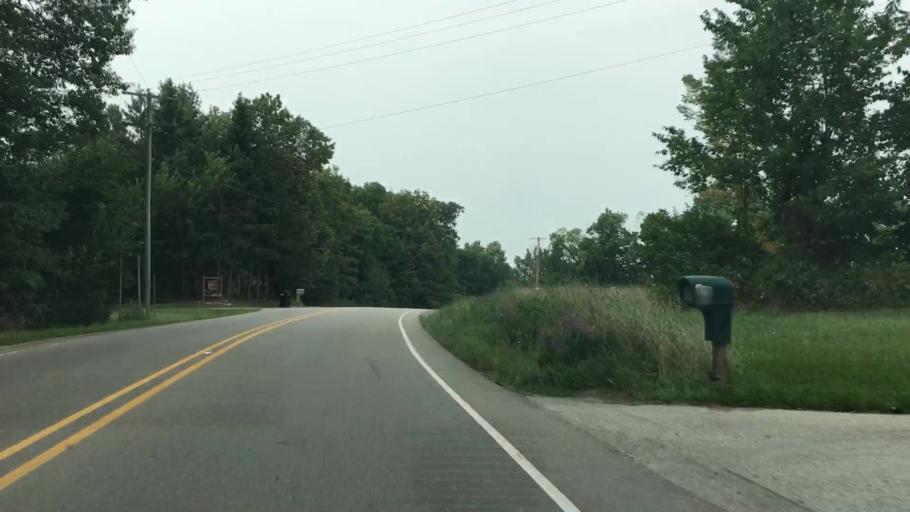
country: US
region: Michigan
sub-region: Ottawa County
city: Hudsonville
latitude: 42.8387
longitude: -85.9004
